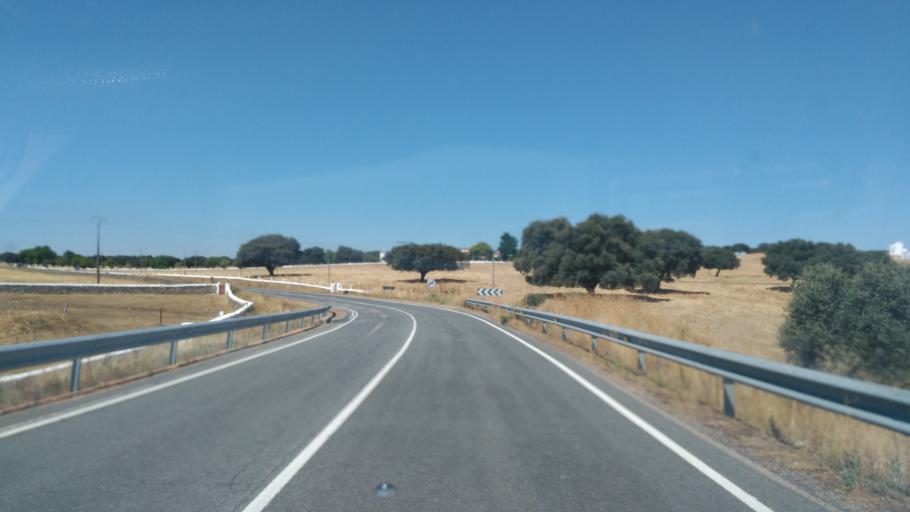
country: ES
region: Castille and Leon
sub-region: Provincia de Salamanca
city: Vecinos
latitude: 40.7867
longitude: -5.8897
